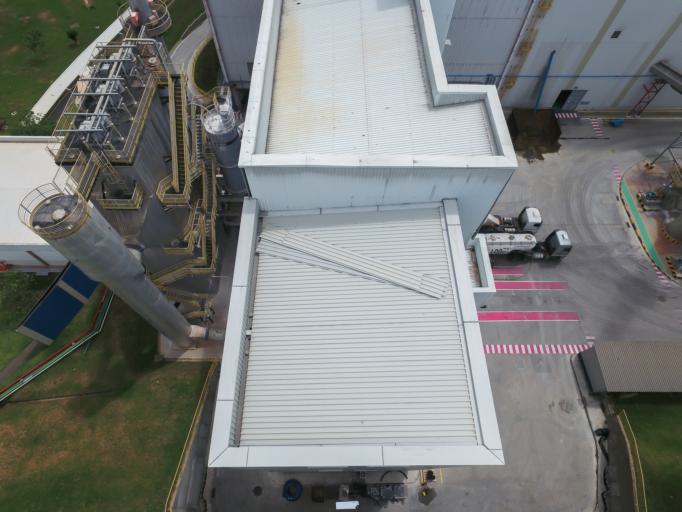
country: BR
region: Rio de Janeiro
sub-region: Seropedica
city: Seropedica
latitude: -22.8691
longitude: -43.6073
